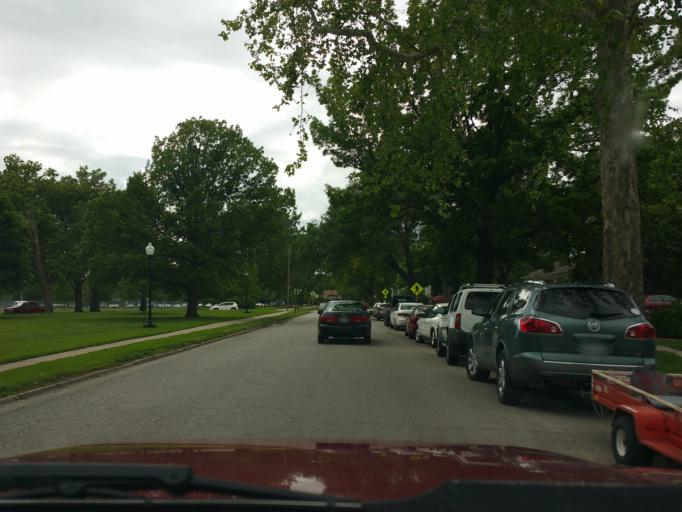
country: US
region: Kansas
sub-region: Riley County
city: Manhattan
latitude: 39.1836
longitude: -96.5735
